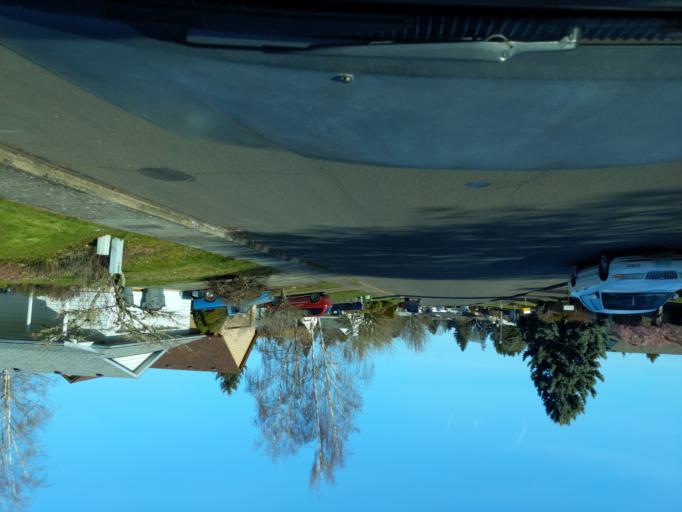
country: US
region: Oregon
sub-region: Yamhill County
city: McMinnville
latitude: 45.2002
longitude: -123.2116
